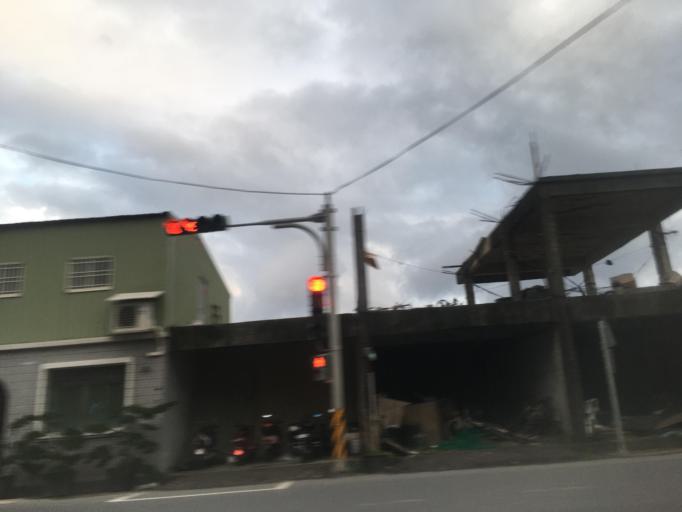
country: TW
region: Taiwan
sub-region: Yilan
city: Yilan
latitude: 24.9009
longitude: 121.8634
